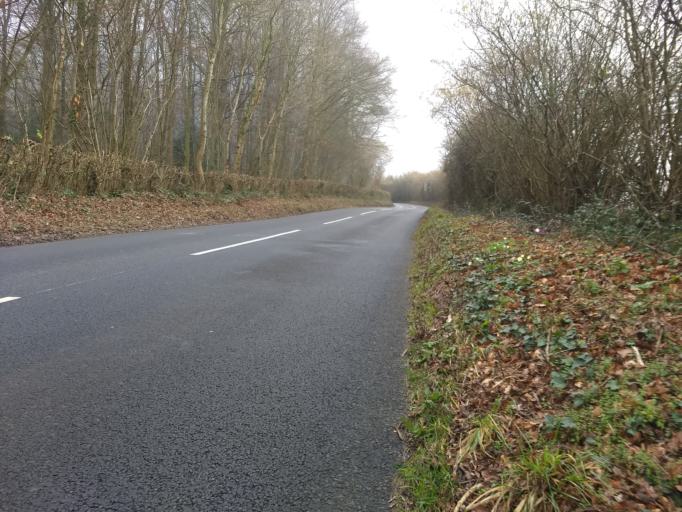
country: GB
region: England
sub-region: Isle of Wight
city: Newchurch
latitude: 50.7020
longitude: -1.2303
